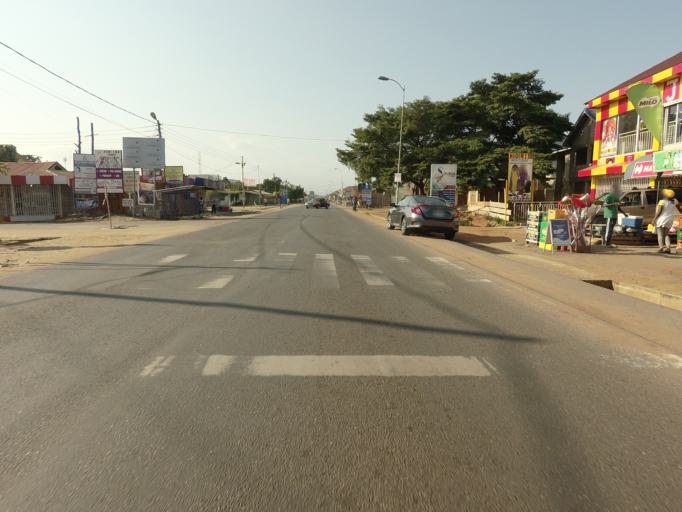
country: GH
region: Greater Accra
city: Nungua
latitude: 5.6337
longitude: -0.0762
